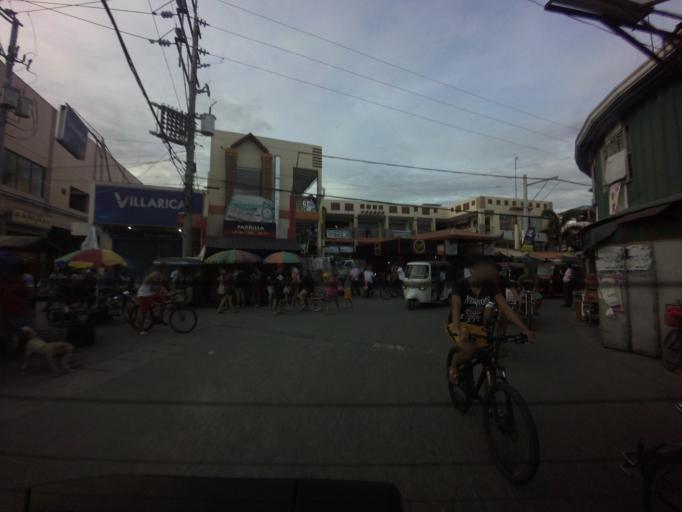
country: PH
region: Central Luzon
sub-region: Province of Bulacan
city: Obando
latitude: 14.7121
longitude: 120.9351
